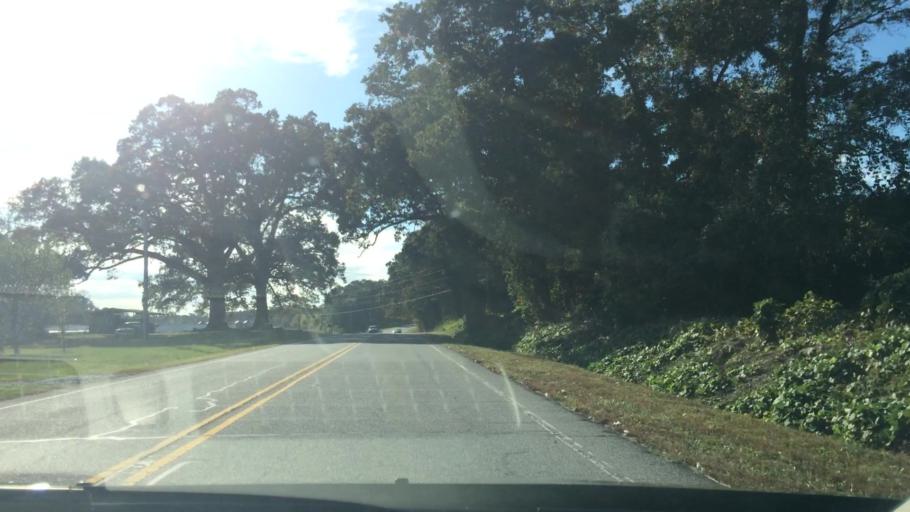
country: US
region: North Carolina
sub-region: Greene County
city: Snow Hill
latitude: 35.4567
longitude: -77.7127
